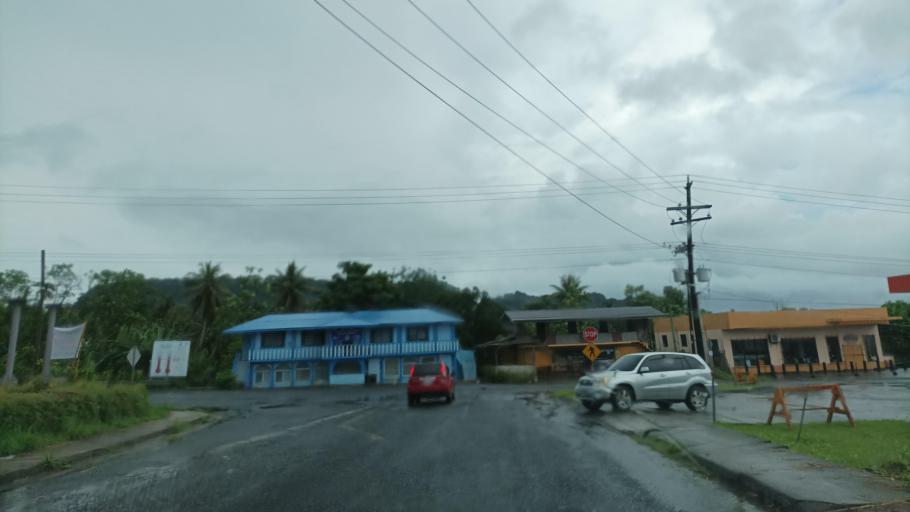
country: FM
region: Pohnpei
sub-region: Kolonia Municipality
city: Kolonia
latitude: 6.9628
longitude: 158.2113
